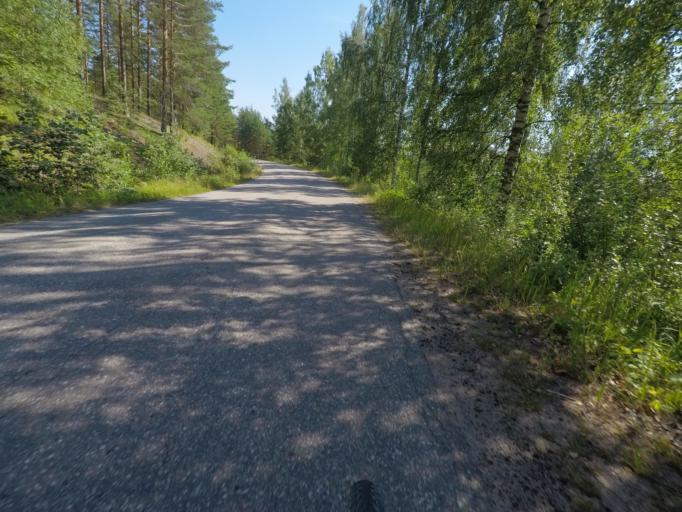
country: FI
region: Southern Savonia
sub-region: Mikkeli
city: Puumala
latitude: 61.4218
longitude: 28.1061
